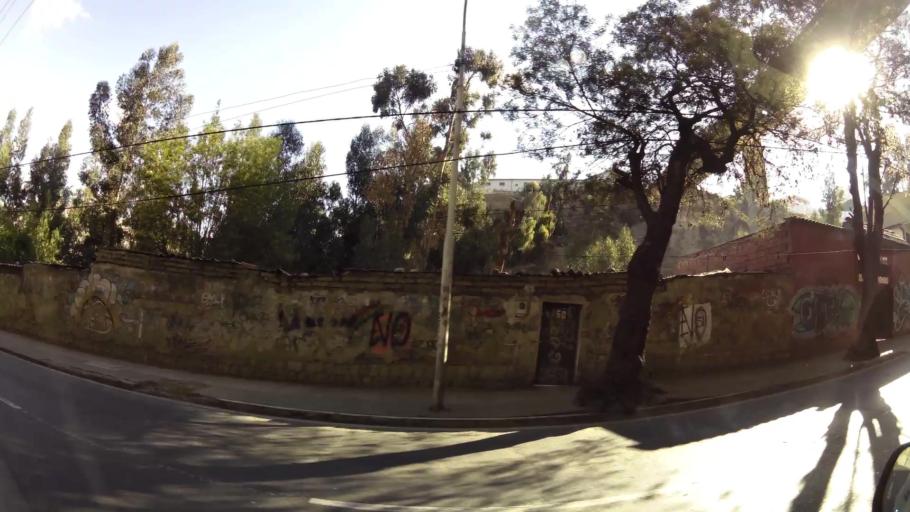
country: BO
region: La Paz
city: La Paz
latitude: -16.5164
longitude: -68.1169
